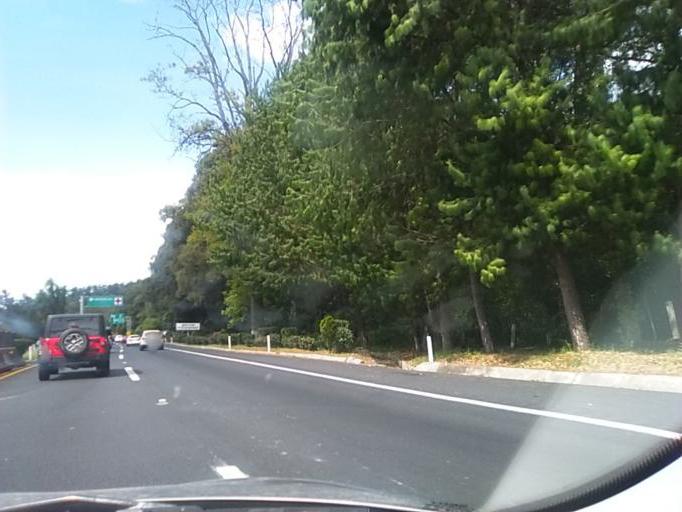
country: MX
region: Morelos
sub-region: Cuernavaca
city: Villa Santiago
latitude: 19.0137
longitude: -99.1607
